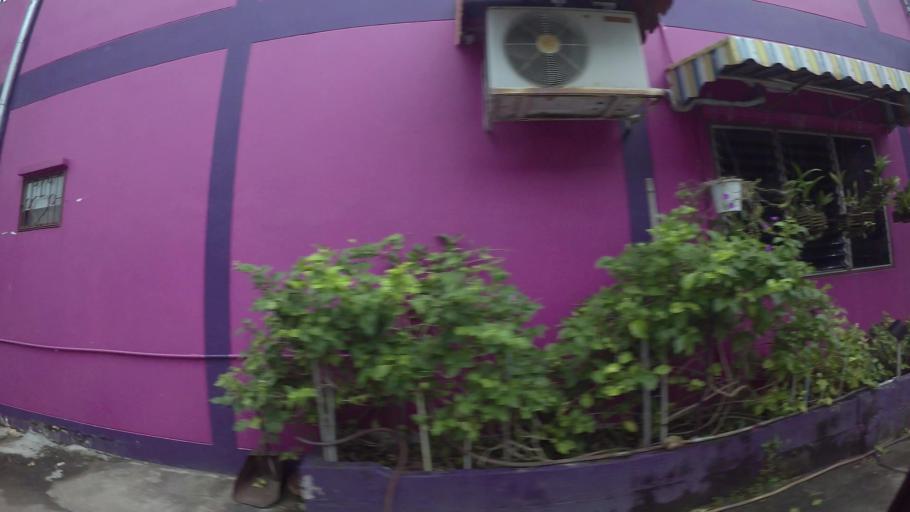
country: TH
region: Chon Buri
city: Si Racha
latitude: 13.2050
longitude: 100.9484
